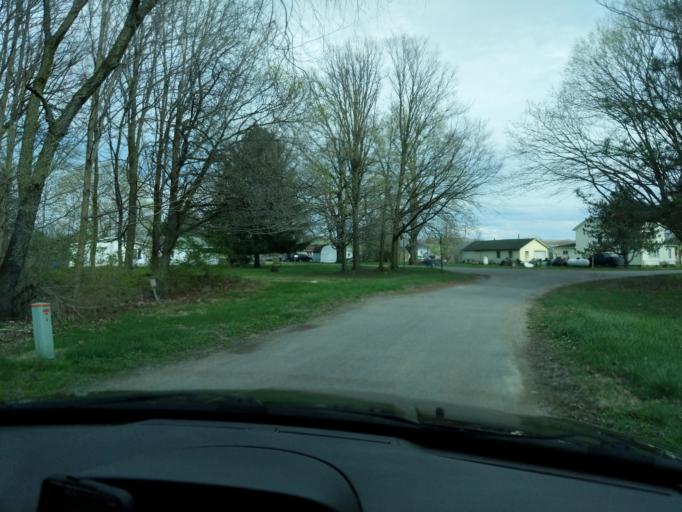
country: US
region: Ohio
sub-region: Logan County
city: West Liberty
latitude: 40.1935
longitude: -83.6798
